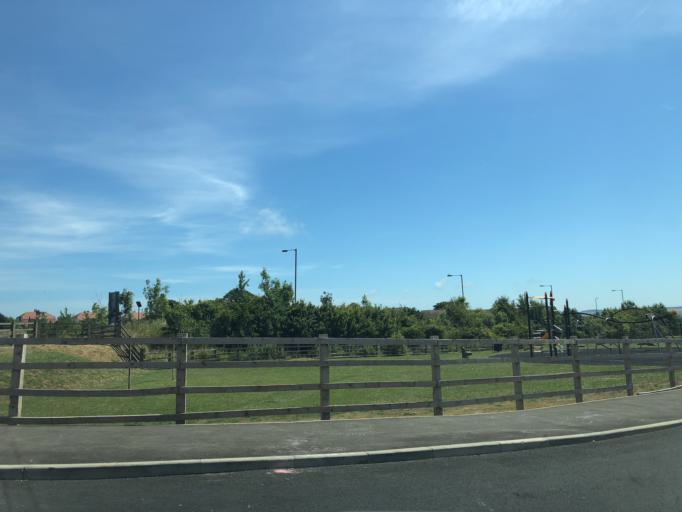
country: GB
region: England
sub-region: North Yorkshire
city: Scarborough
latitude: 54.2467
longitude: -0.3854
